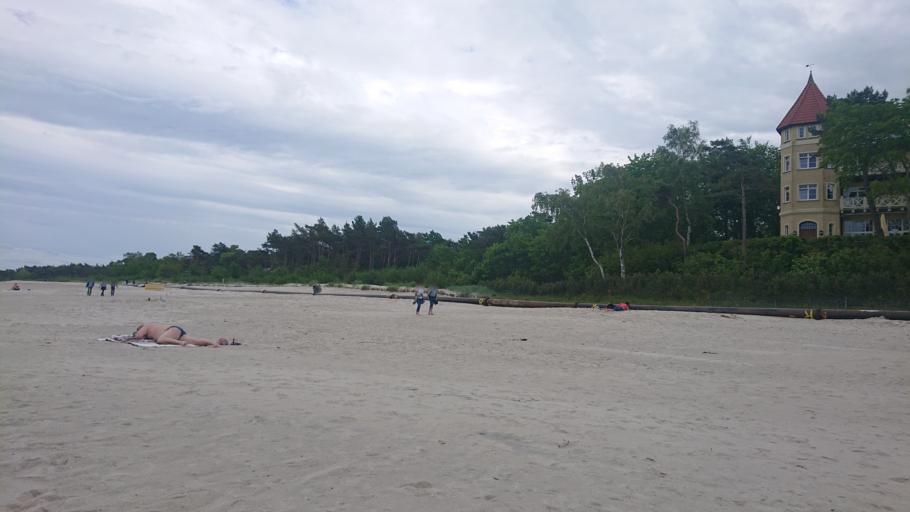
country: PL
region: Pomeranian Voivodeship
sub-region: Powiat leborski
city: Leba
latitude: 54.7687
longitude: 17.5633
